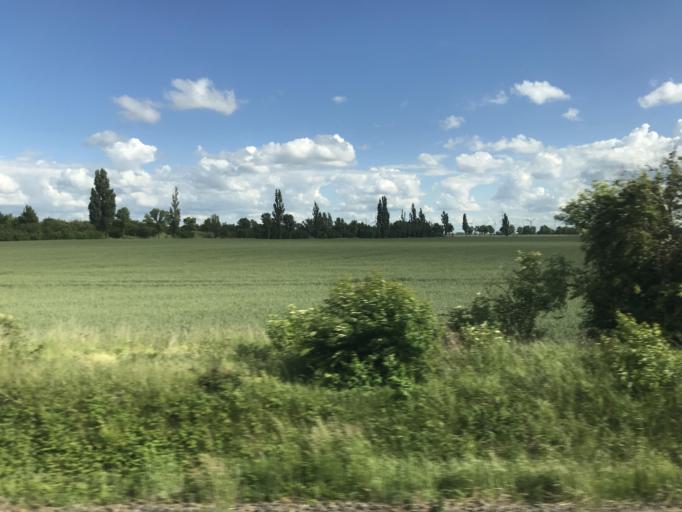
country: DE
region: Saxony-Anhalt
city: Reussen
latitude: 51.5202
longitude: 12.1330
